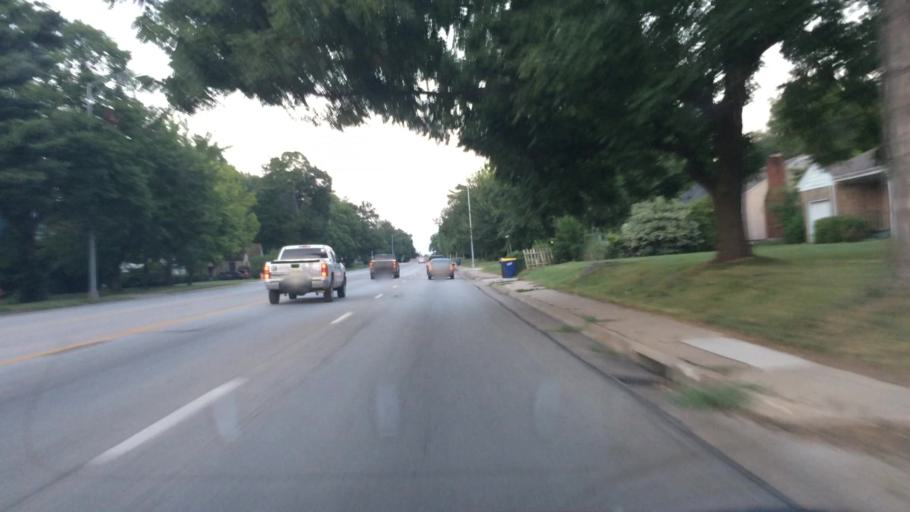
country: US
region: Missouri
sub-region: Greene County
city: Springfield
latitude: 37.1820
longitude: -93.2844
